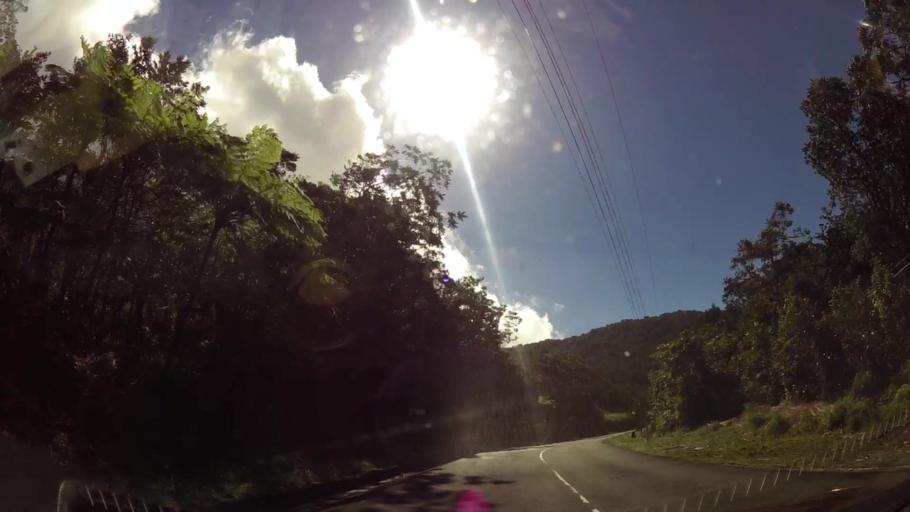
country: DM
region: Saint Paul
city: Pont Casse
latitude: 15.3764
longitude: -61.3438
